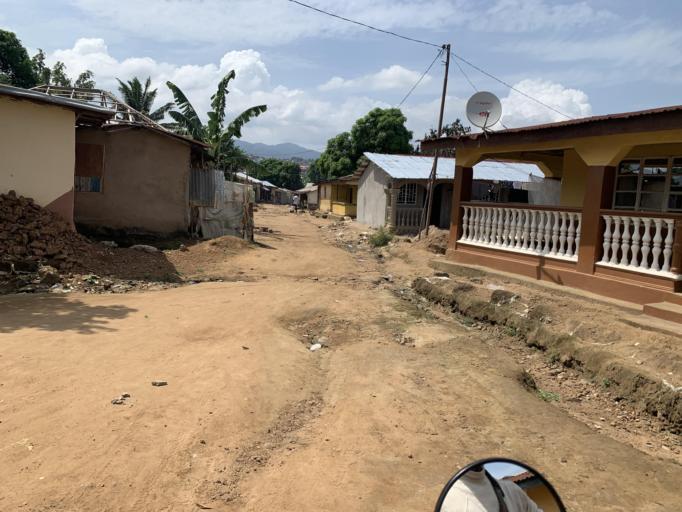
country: SL
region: Western Area
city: Hastings
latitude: 8.4104
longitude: -13.1336
